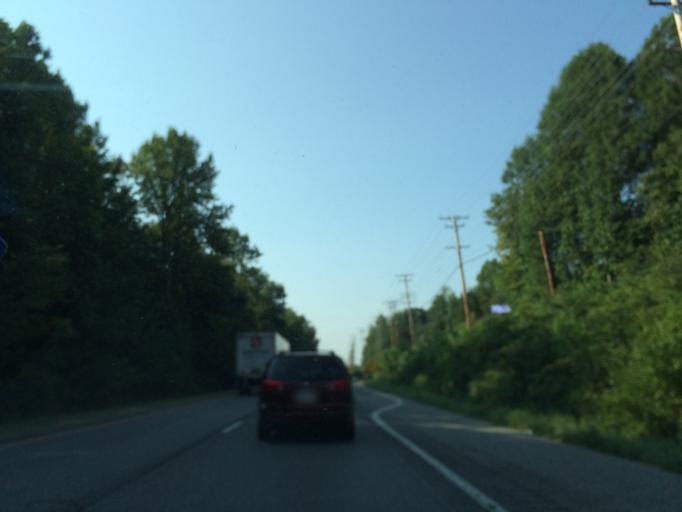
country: US
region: Maryland
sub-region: Prince George's County
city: Bowie
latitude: 38.9277
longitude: -76.7171
